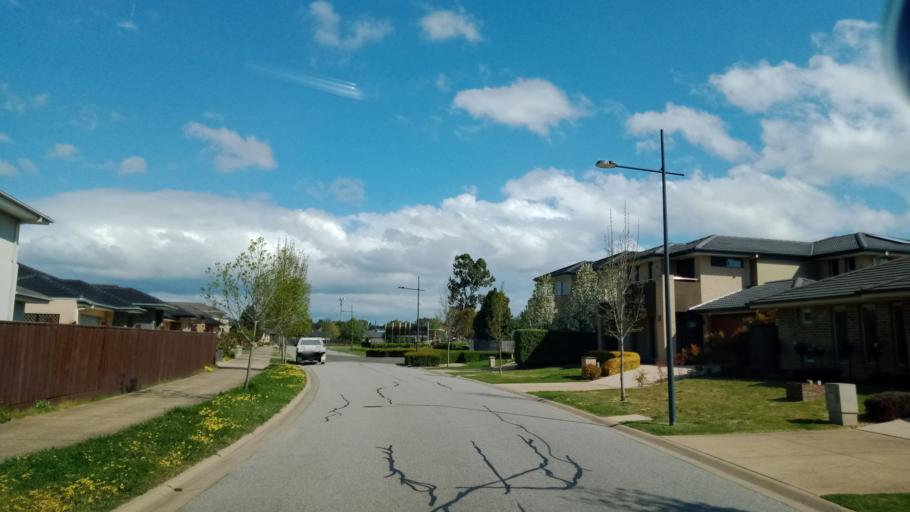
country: AU
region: Victoria
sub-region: Frankston
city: Sandhurst
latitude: -38.0847
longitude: 145.2106
